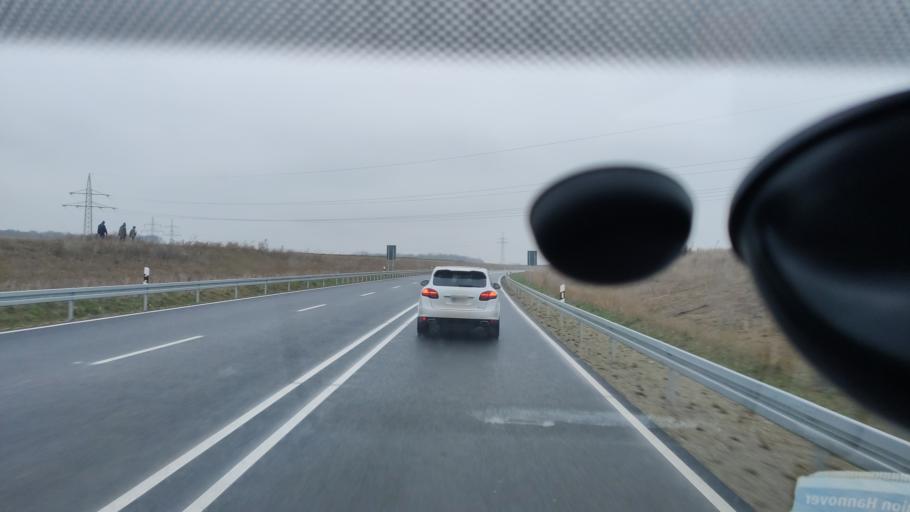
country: DE
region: Lower Saxony
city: Hemmingen
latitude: 52.2965
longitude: 9.7233
